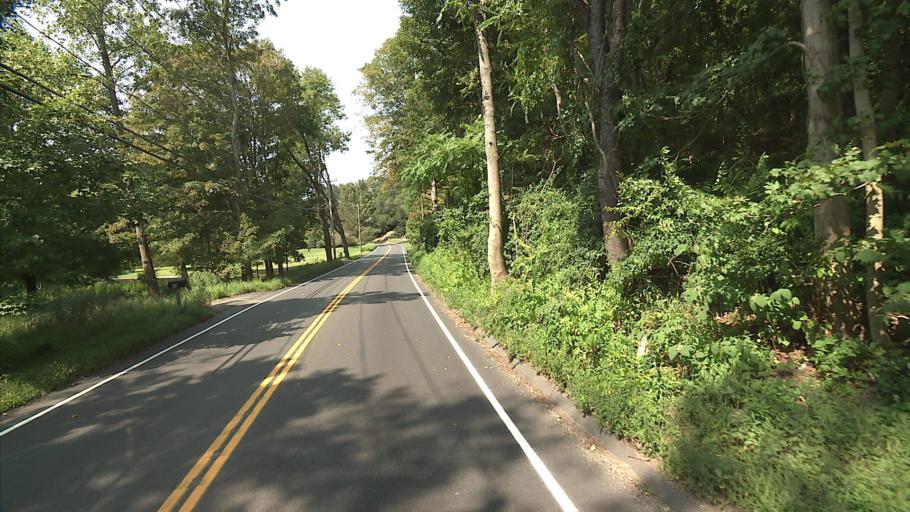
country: US
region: Connecticut
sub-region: Fairfield County
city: Bethel
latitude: 41.3613
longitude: -73.3830
